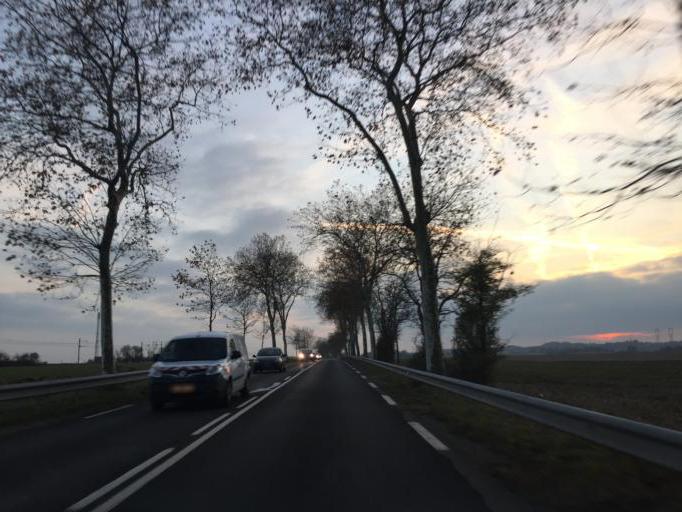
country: FR
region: Rhone-Alpes
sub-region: Departement de l'Ain
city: Perouges
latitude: 45.8792
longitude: 5.1634
